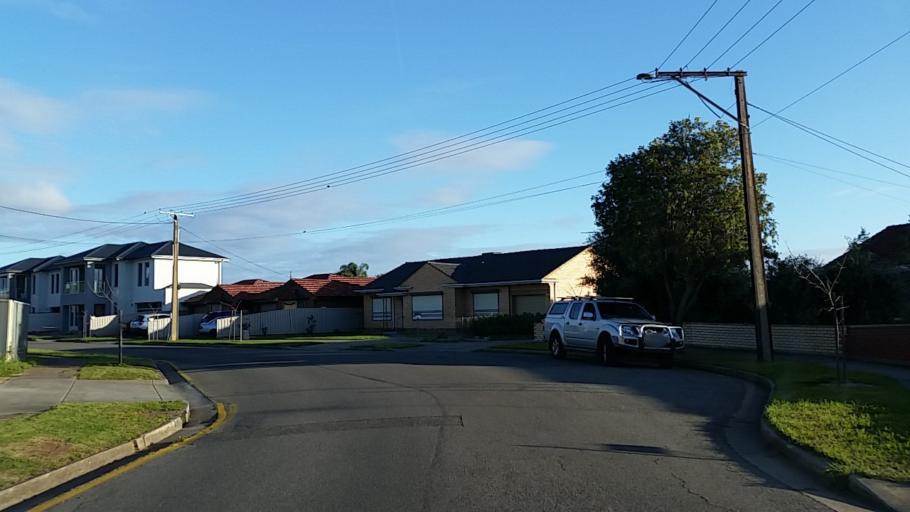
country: AU
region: South Australia
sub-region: Charles Sturt
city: Findon
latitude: -34.8949
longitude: 138.5363
